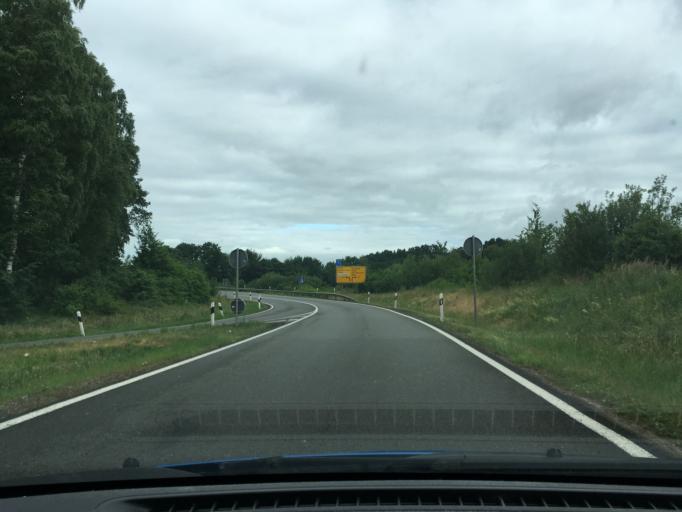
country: DE
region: Lower Saxony
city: Wenzendorf
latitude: 53.3718
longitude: 9.8071
